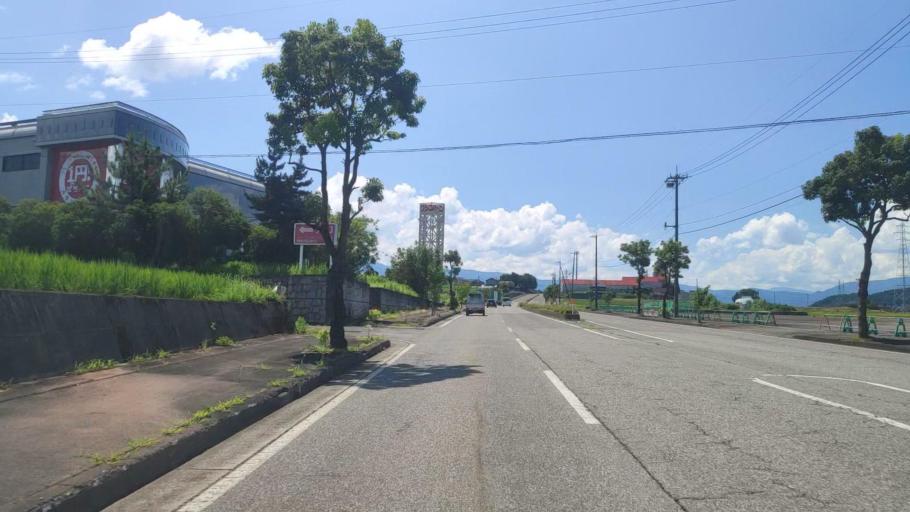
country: JP
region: Fukui
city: Katsuyama
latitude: 36.0430
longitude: 136.5181
